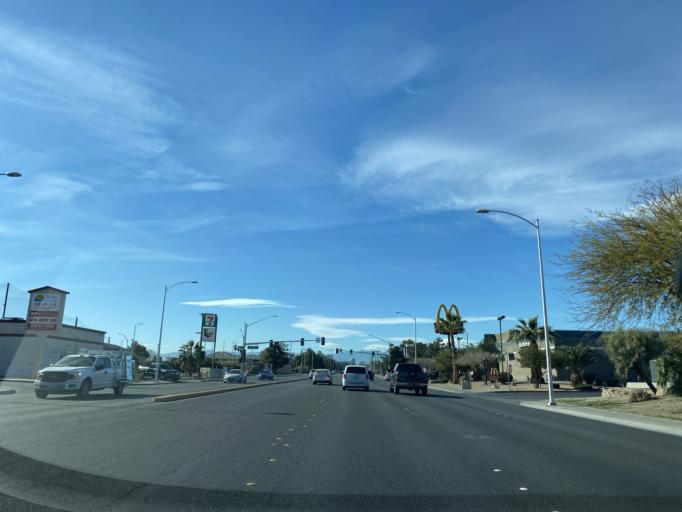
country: US
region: Nevada
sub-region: Clark County
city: North Las Vegas
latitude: 36.1735
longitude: -115.0970
